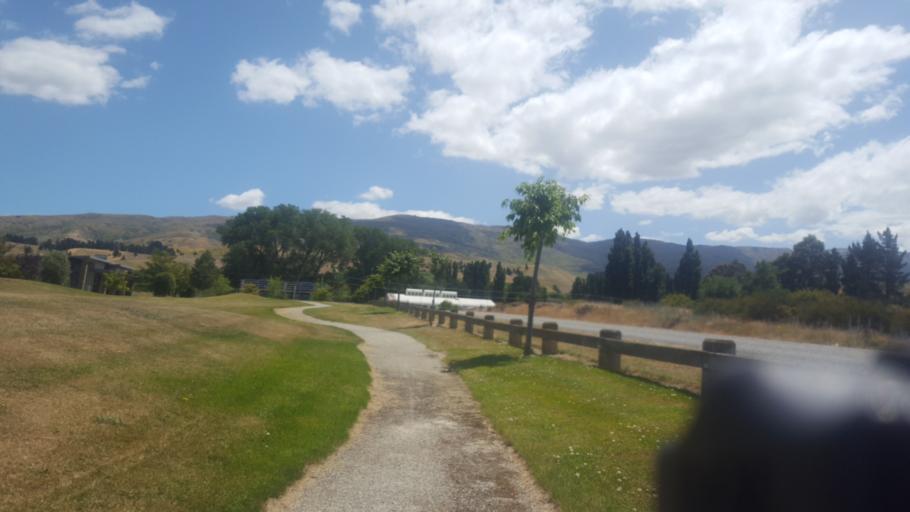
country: NZ
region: Otago
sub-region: Queenstown-Lakes District
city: Wanaka
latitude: -45.0300
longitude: 169.2005
